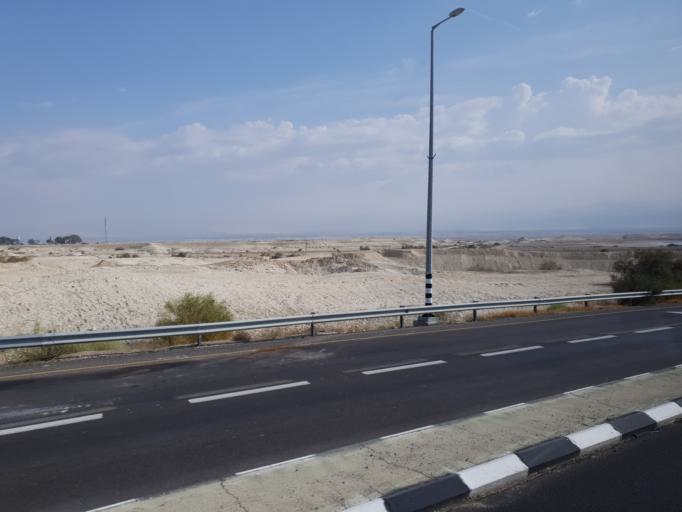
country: PS
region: West Bank
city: Jericho
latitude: 31.7989
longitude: 35.4910
